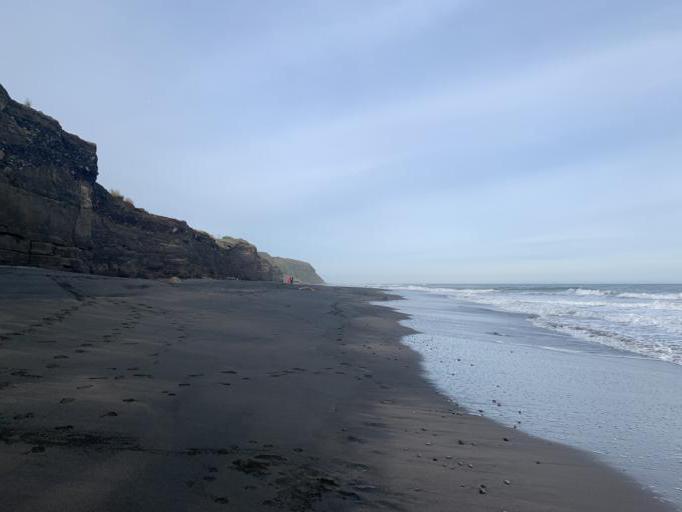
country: NZ
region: Taranaki
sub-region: South Taranaki District
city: Opunake
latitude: -39.5645
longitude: 174.0551
